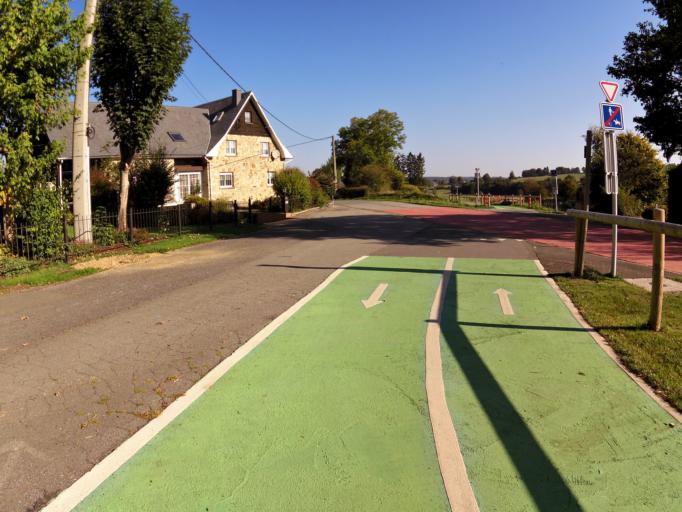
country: BE
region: Wallonia
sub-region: Province de Liege
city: Ambleve
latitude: 50.3377
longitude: 6.1196
